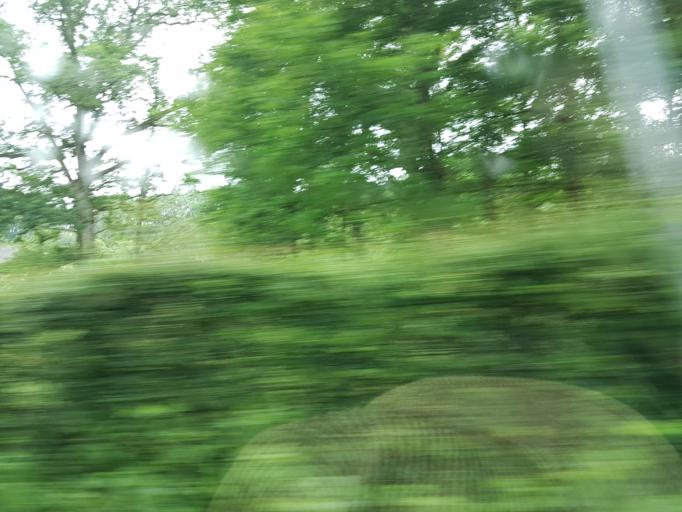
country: FR
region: Bourgogne
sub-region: Departement de la Nievre
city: Corbigny
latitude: 47.1801
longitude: 3.7416
